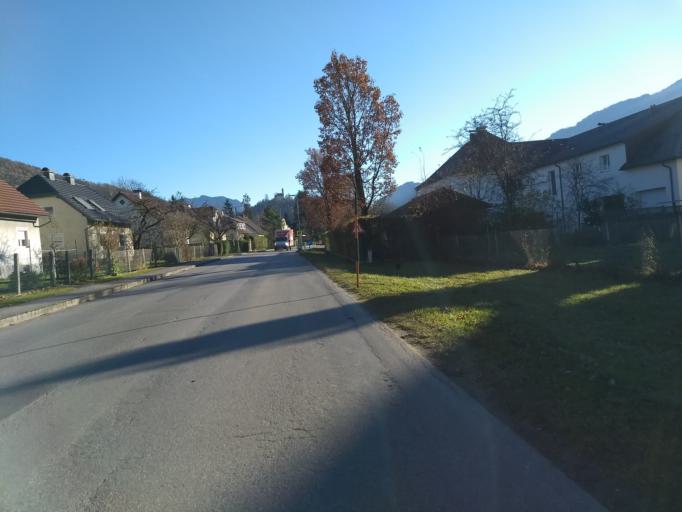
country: AT
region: Upper Austria
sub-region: Politischer Bezirk Kirchdorf an der Krems
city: Micheldorf in Oberoesterreich
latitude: 47.8861
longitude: 14.1320
